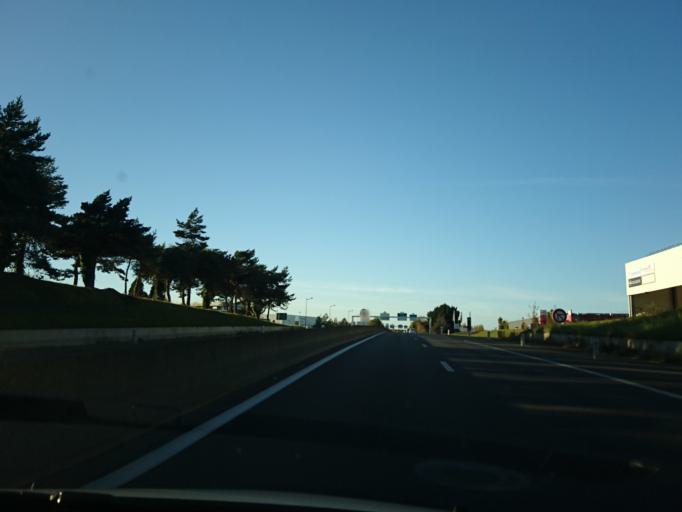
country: FR
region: Brittany
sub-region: Departement des Cotes-d'Armor
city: Langueux
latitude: 48.5058
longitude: -2.7339
